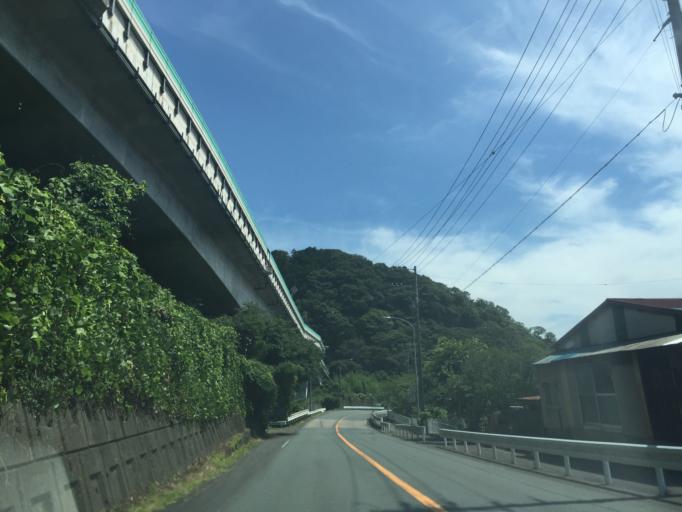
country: JP
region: Shizuoka
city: Kanaya
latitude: 34.8026
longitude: 138.0764
